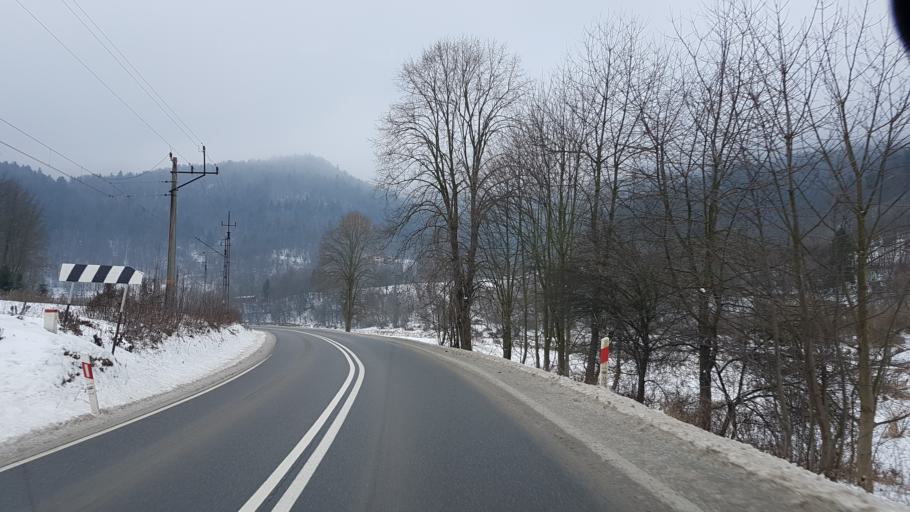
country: PL
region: Lesser Poland Voivodeship
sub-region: Powiat nowosadecki
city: Piwniczna-Zdroj
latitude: 49.3938
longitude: 20.7494
